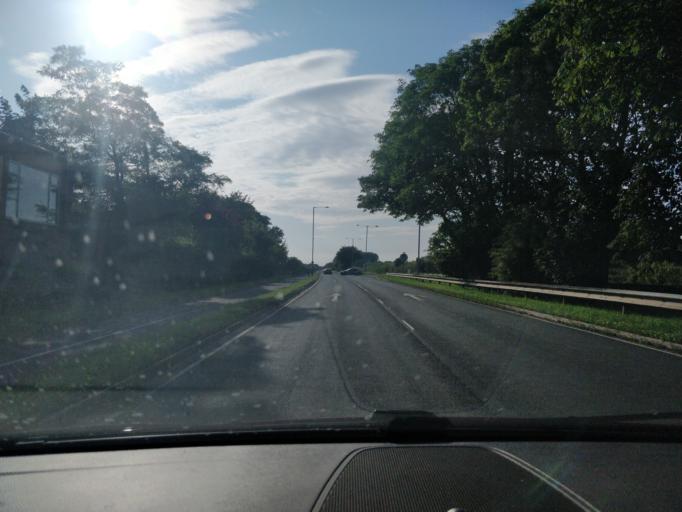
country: GB
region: England
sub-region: Lancashire
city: Banks
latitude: 53.6688
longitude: -2.9050
